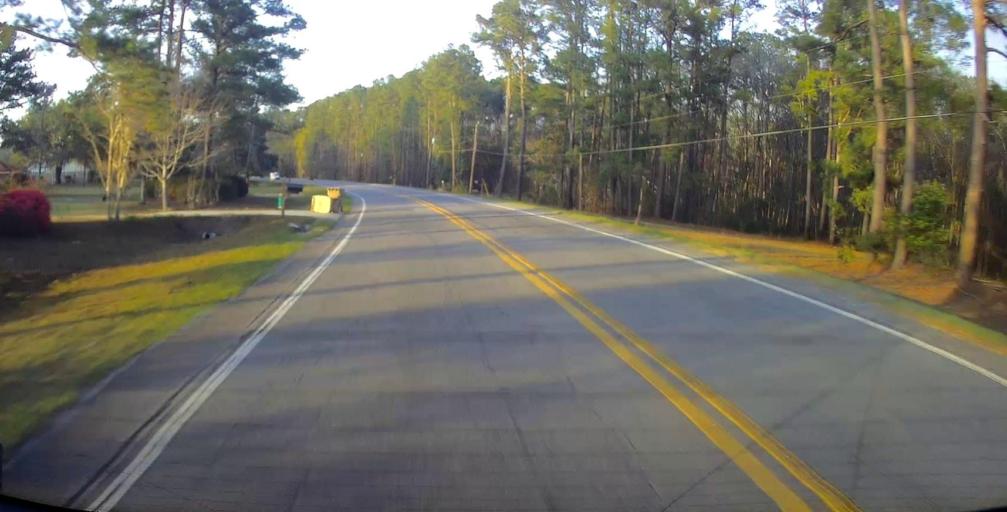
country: US
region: Georgia
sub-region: Chatham County
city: Bloomingdale
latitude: 32.1641
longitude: -81.3850
